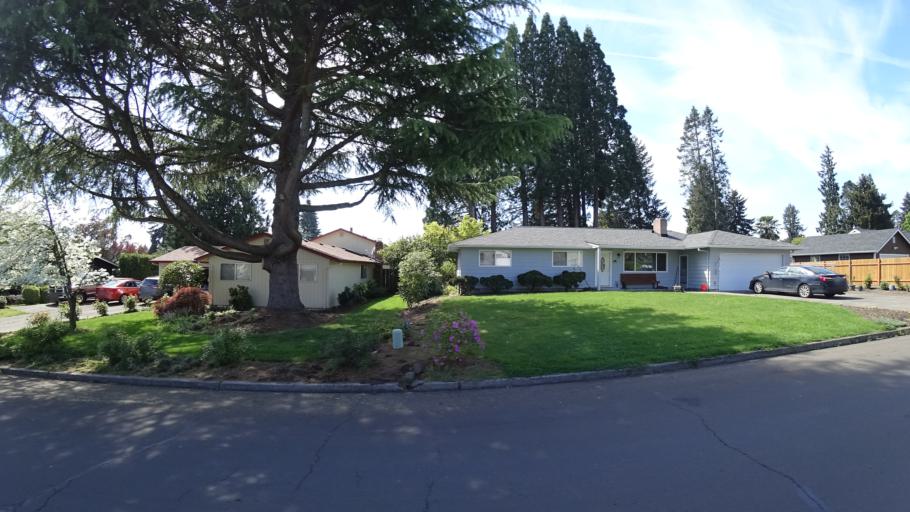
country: US
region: Oregon
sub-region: Washington County
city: Hillsboro
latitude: 45.5124
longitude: -122.9583
